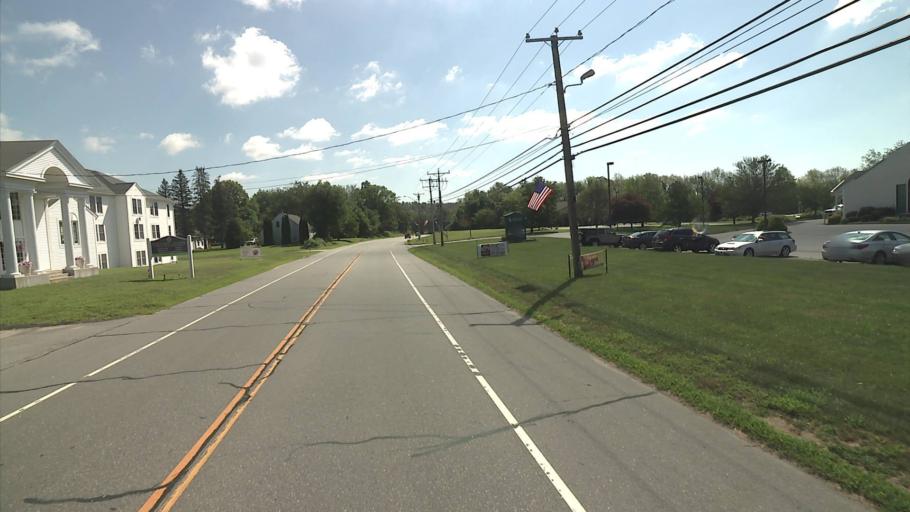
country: US
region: Connecticut
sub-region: Windham County
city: Plainfield Village
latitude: 41.6978
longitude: -71.9950
